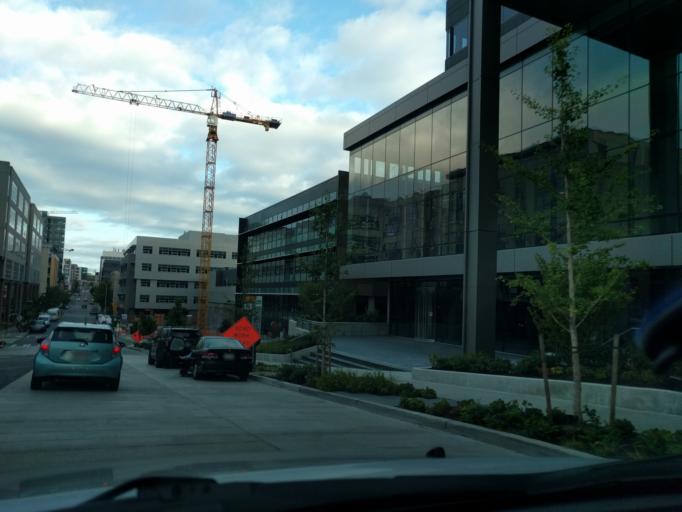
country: US
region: Washington
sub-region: King County
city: Seattle
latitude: 47.6232
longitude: -122.3347
